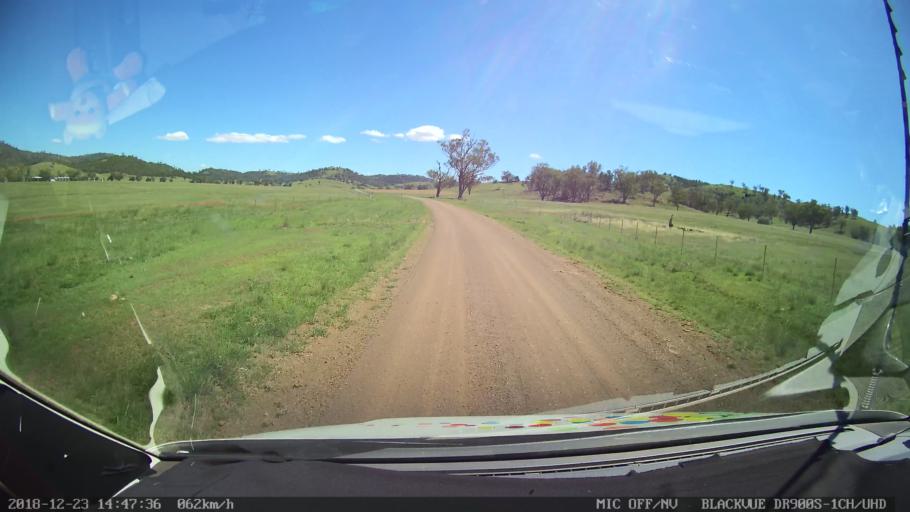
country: AU
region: New South Wales
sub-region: Tamworth Municipality
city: Manilla
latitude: -30.6551
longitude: 150.8733
